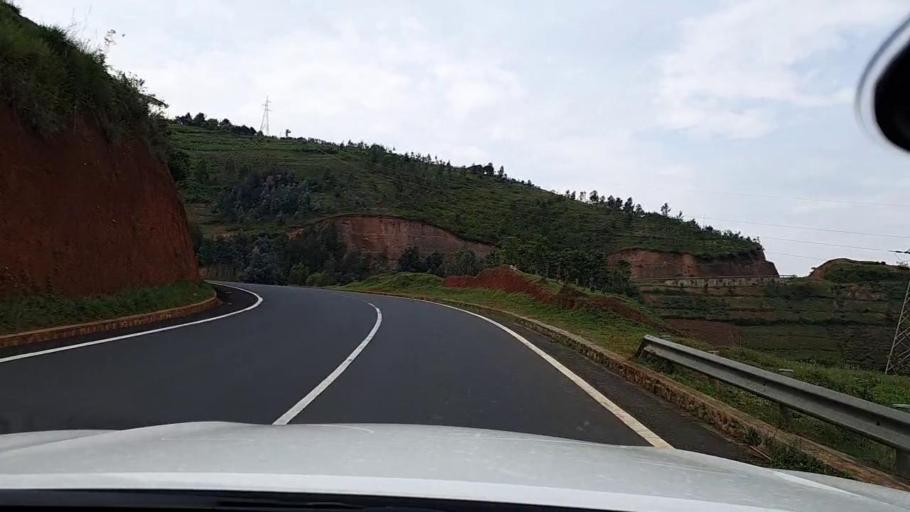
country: RW
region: Western Province
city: Kibuye
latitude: -2.1669
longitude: 29.2920
